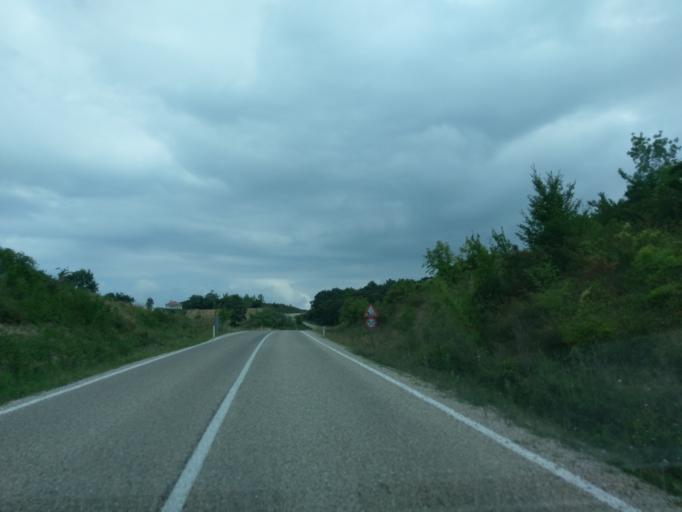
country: TR
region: Sinop
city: Erfelek
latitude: 41.9665
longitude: 34.8360
